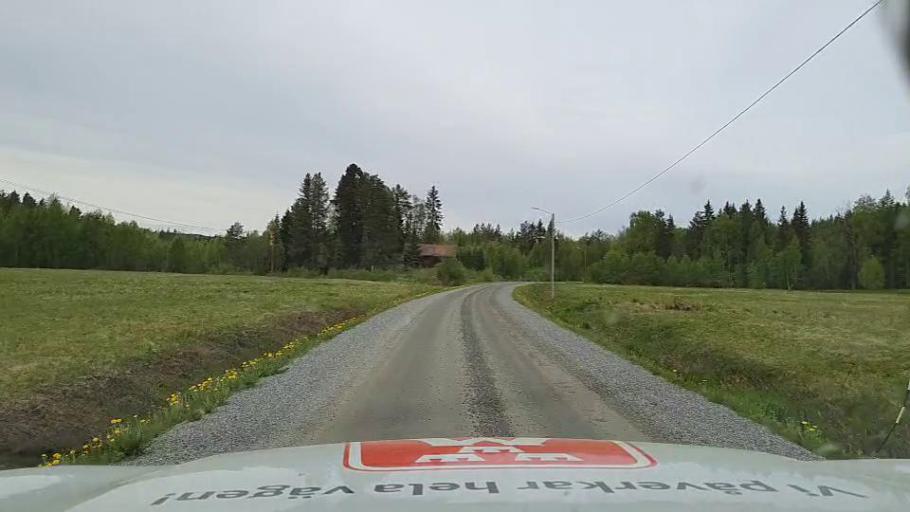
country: SE
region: Jaemtland
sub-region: Braecke Kommun
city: Braecke
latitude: 62.4537
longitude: 14.9154
